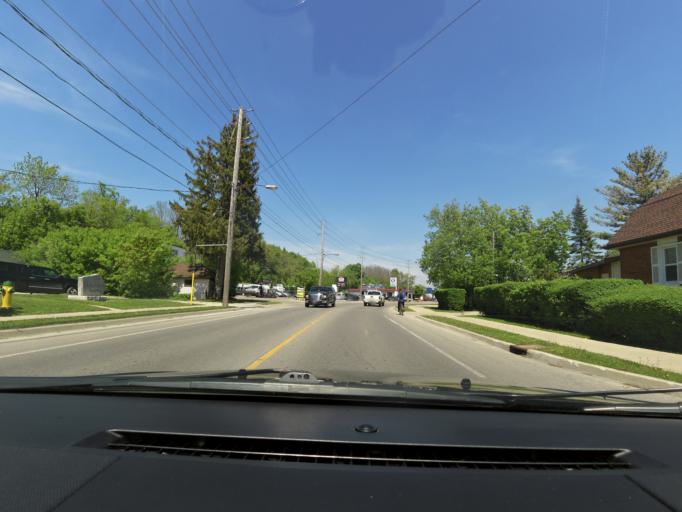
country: CA
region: Ontario
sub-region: Wellington County
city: Guelph
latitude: 43.5543
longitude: -80.2332
